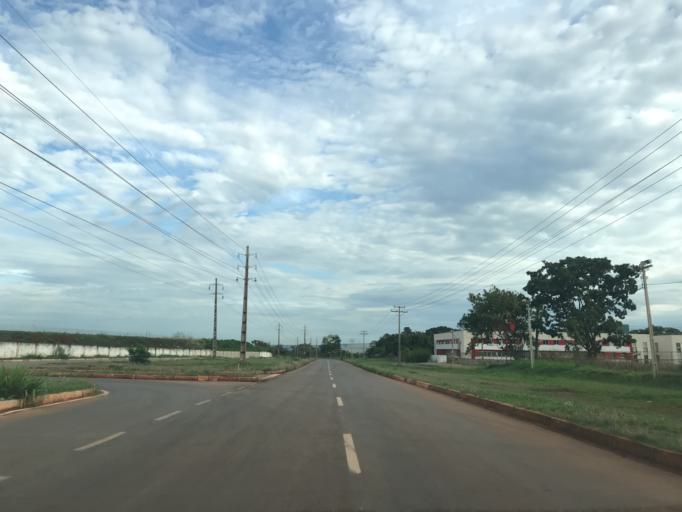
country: BR
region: Federal District
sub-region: Brasilia
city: Brasilia
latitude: -15.7739
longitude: -47.8952
